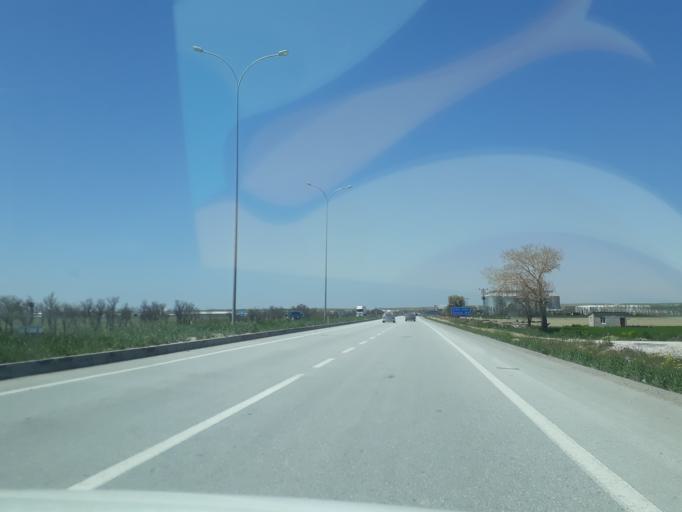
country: TR
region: Konya
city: Karapinar
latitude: 37.7151
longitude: 33.5105
